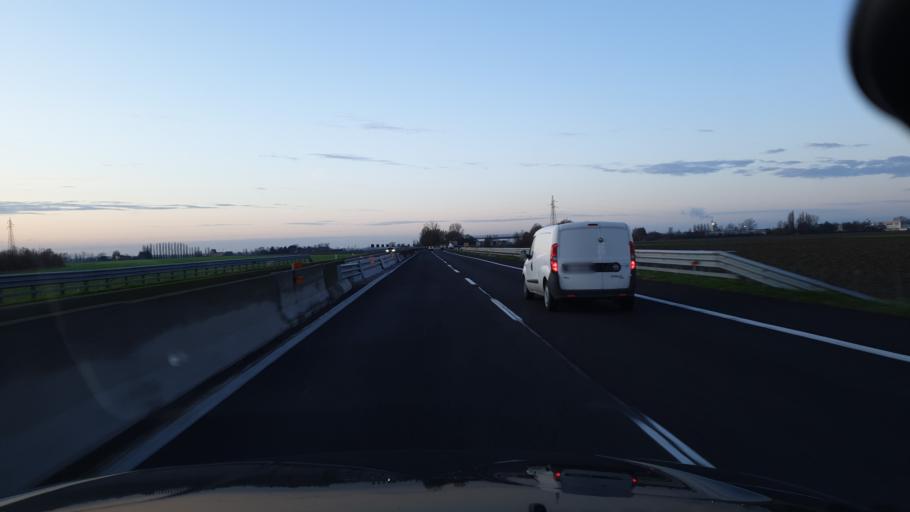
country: IT
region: Veneto
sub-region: Provincia di Rovigo
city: Fiesso Umbertiano
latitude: 44.9511
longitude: 11.6374
